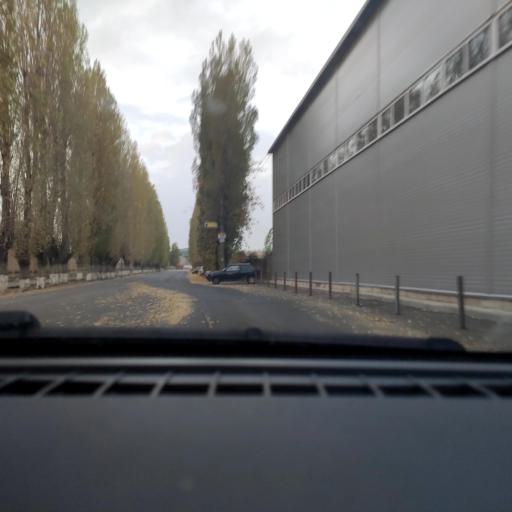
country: RU
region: Voronezj
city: Voronezh
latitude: 51.6501
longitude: 39.2795
